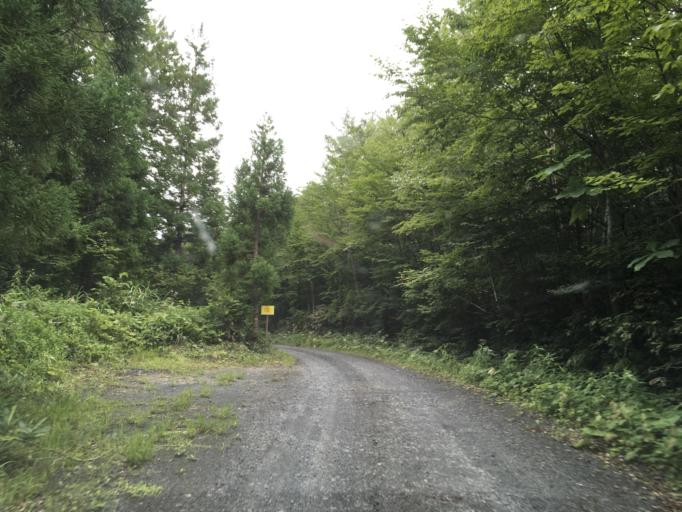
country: JP
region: Iwate
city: Ichinoseki
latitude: 38.9504
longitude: 140.8537
